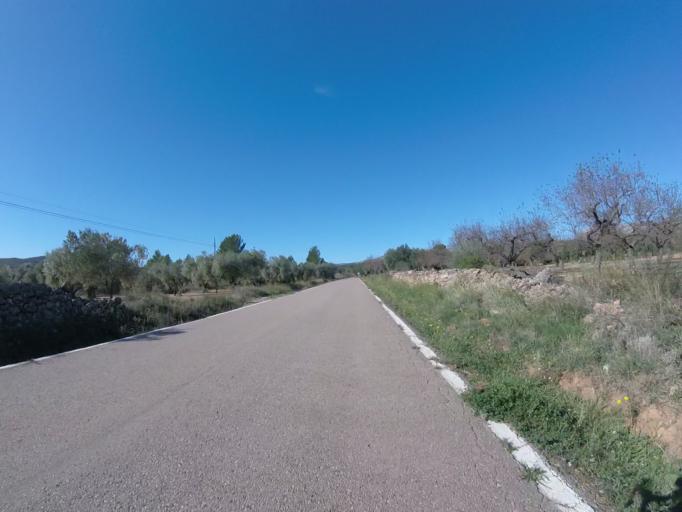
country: ES
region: Valencia
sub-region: Provincia de Castello
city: Chert/Xert
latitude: 40.4505
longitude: 0.1168
